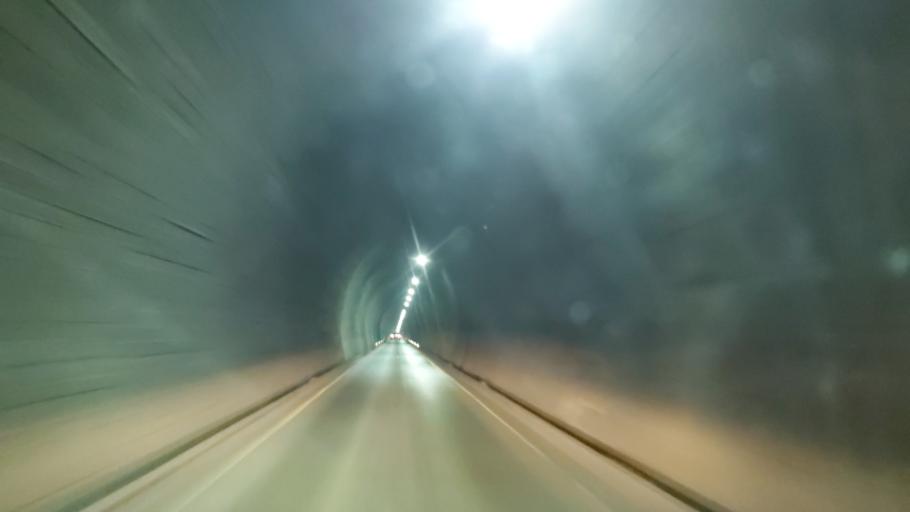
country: CL
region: Araucania
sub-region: Provincia de Cautin
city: Vilcun
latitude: -38.5402
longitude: -71.5063
